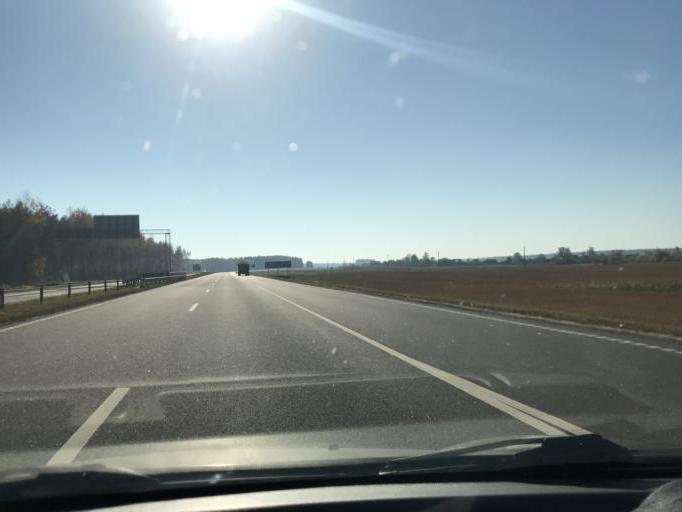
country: BY
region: Mogilev
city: Babruysk
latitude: 53.1388
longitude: 29.3654
